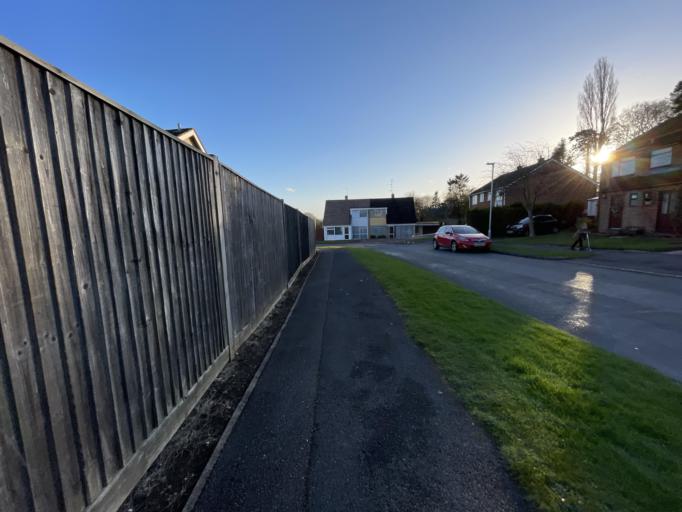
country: GB
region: England
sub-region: West Berkshire
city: Tilehurst
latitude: 51.4492
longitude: -1.0207
